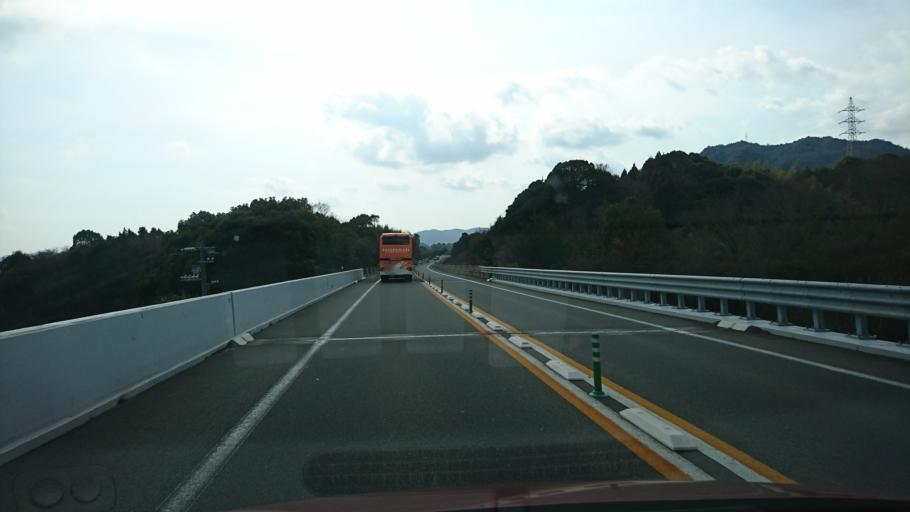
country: JP
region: Hiroshima
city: Innoshima
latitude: 34.2368
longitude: 133.0482
